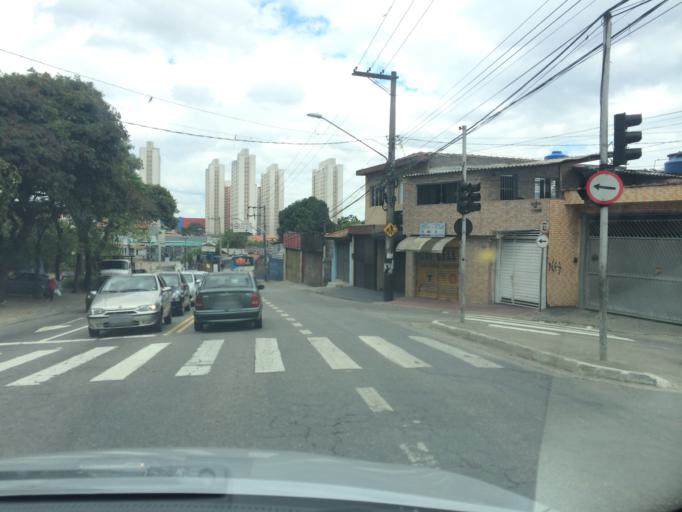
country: BR
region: Sao Paulo
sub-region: Guarulhos
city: Guarulhos
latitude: -23.4389
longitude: -46.5225
